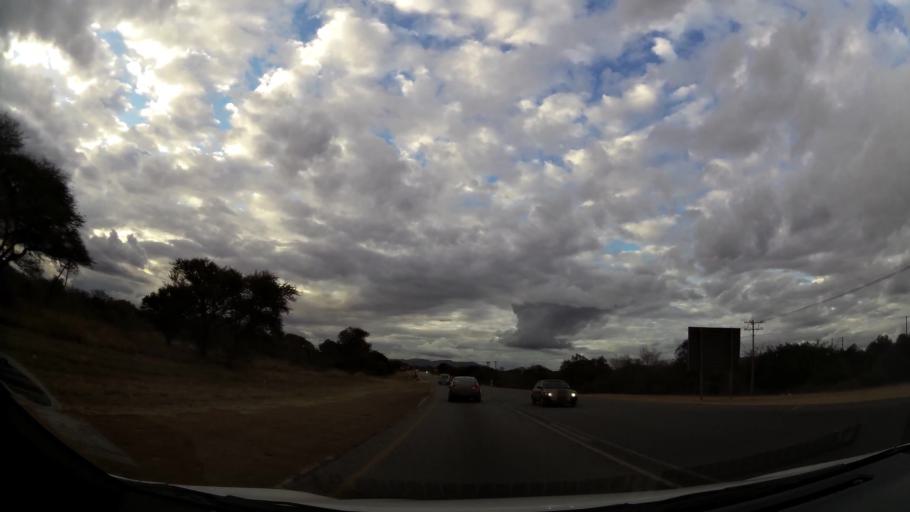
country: ZA
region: Limpopo
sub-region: Waterberg District Municipality
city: Mokopane
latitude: -24.2172
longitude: 29.0055
